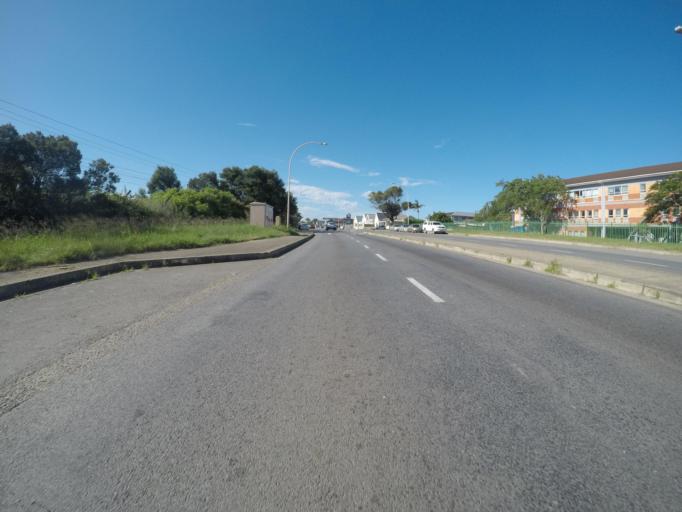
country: ZA
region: Eastern Cape
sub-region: Buffalo City Metropolitan Municipality
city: East London
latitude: -32.9806
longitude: 27.8991
